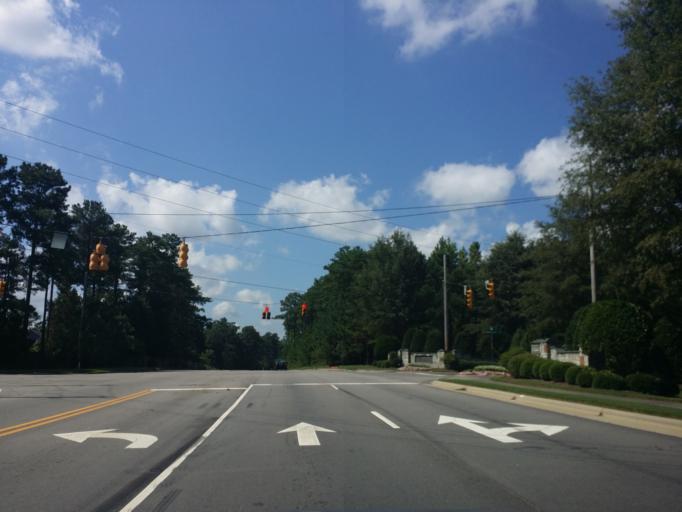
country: US
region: North Carolina
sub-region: Wake County
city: Cary
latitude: 35.9033
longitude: -78.7266
